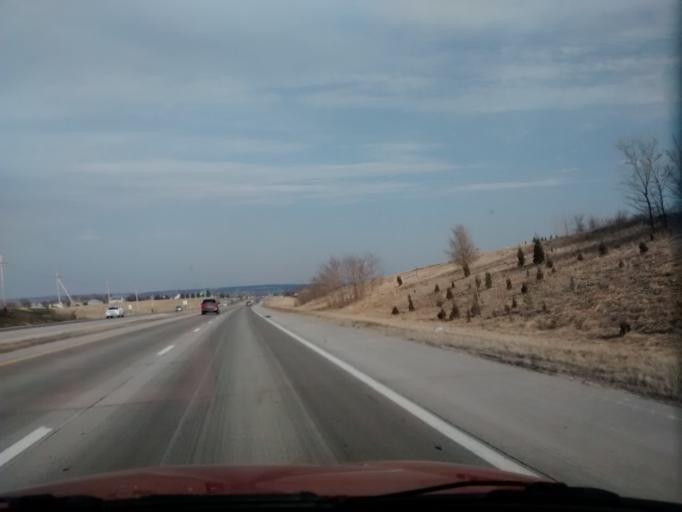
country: US
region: Nebraska
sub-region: Sarpy County
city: Papillion
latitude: 41.1398
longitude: -95.9951
